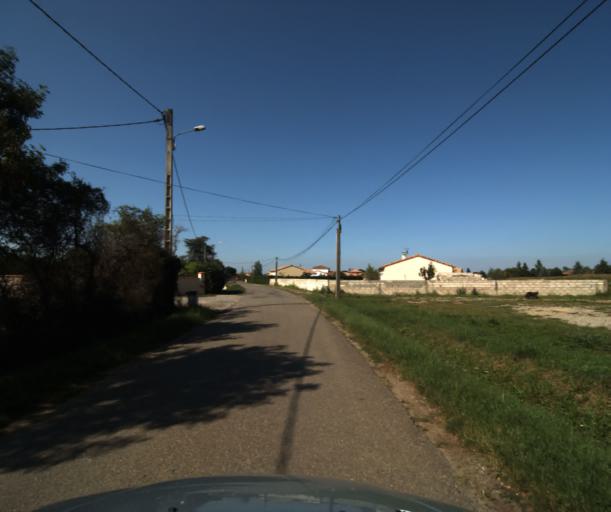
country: FR
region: Midi-Pyrenees
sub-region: Departement de la Haute-Garonne
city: Lacasse
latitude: 43.3865
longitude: 1.2584
